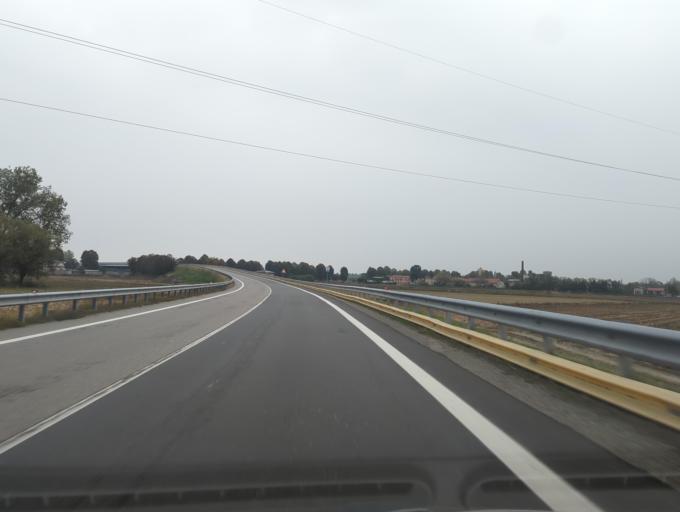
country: IT
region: Piedmont
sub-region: Provincia di Novara
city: Romentino
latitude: 45.4736
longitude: 8.7146
